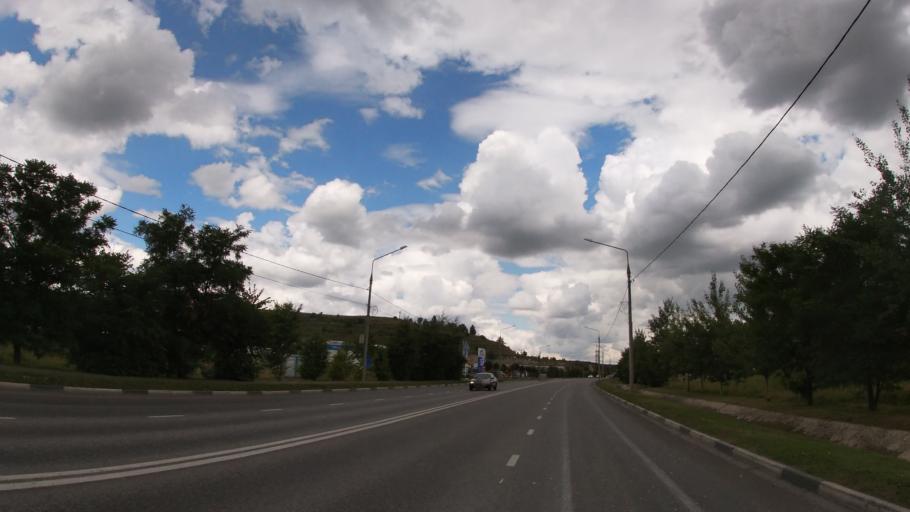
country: RU
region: Belgorod
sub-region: Belgorodskiy Rayon
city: Belgorod
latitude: 50.6139
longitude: 36.6133
